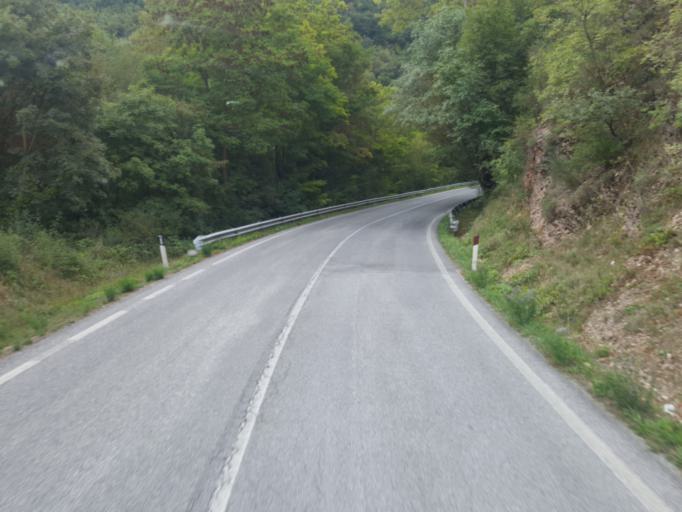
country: IT
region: The Marches
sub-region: Provincia di Ancona
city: Fabriano
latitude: 43.3225
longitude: 12.8381
